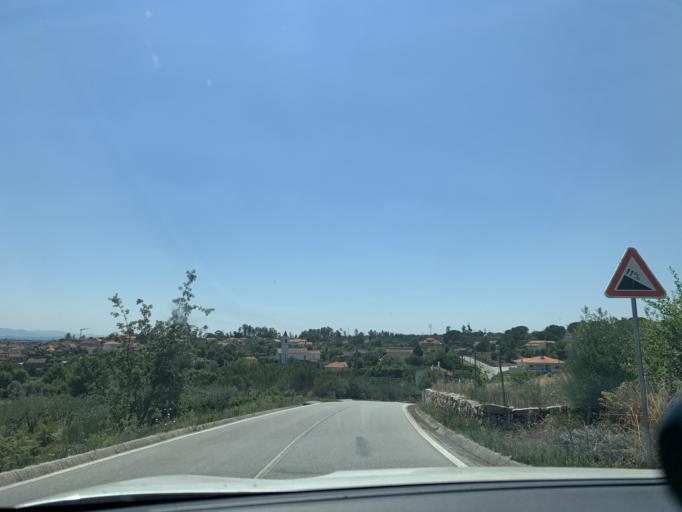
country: PT
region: Viseu
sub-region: Mangualde
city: Mangualde
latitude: 40.5497
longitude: -7.7440
